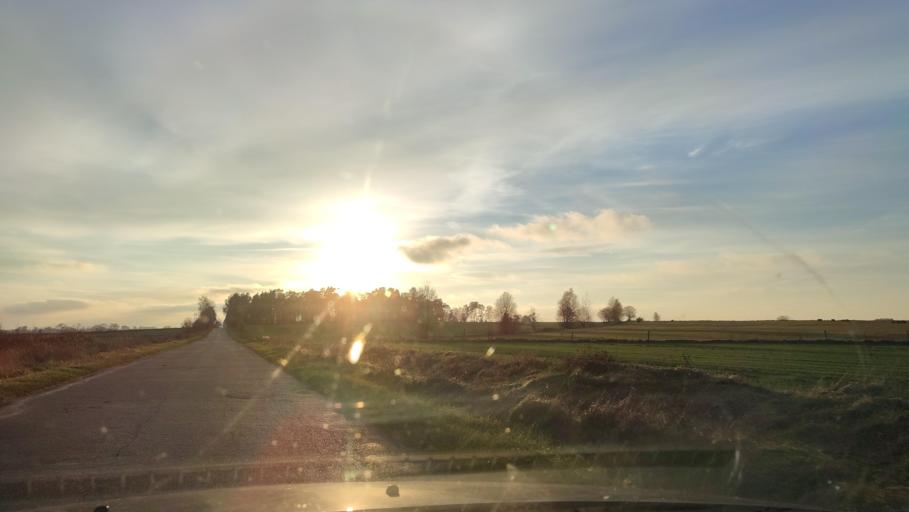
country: PL
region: Masovian Voivodeship
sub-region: Powiat mlawski
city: Dzierzgowo
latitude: 53.2573
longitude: 20.6011
